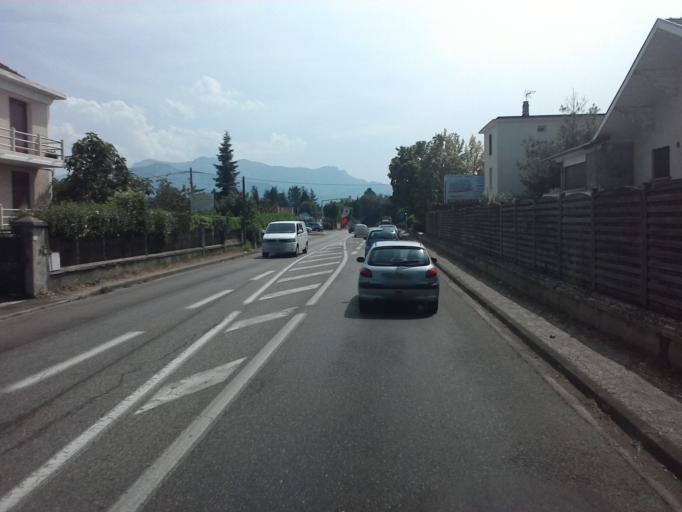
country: FR
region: Rhone-Alpes
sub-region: Departement de l'Isere
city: Saint-Jean-de-Moirans
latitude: 45.3505
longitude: 5.5960
